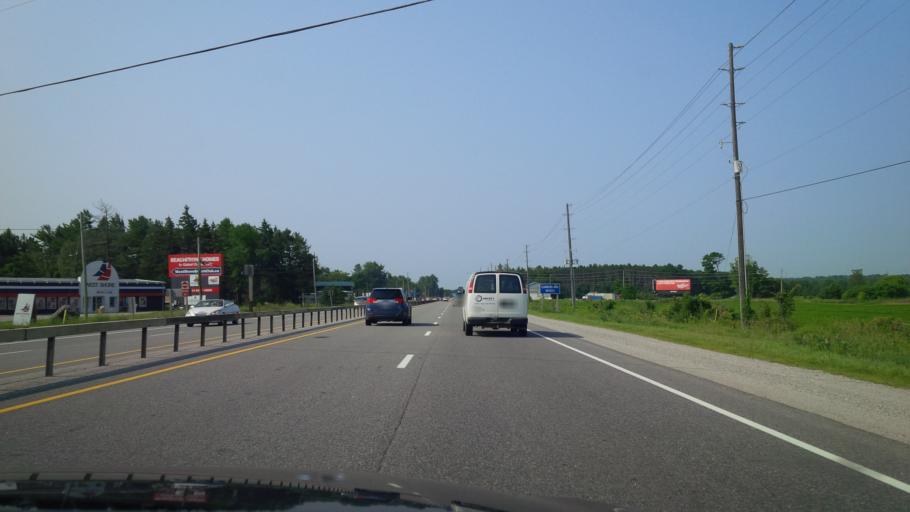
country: CA
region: Ontario
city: Orillia
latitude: 44.7152
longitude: -79.3816
